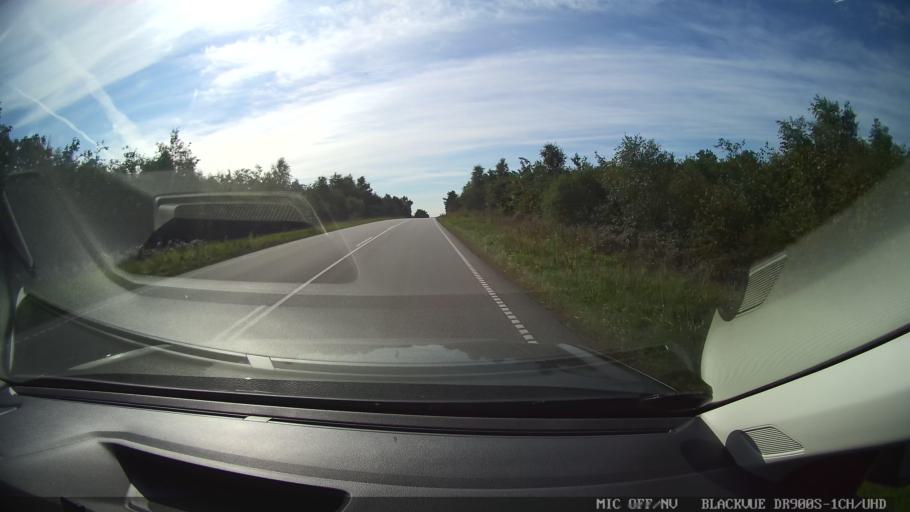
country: DK
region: North Denmark
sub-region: Mariagerfjord Kommune
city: Hadsund
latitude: 56.7538
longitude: 10.0716
